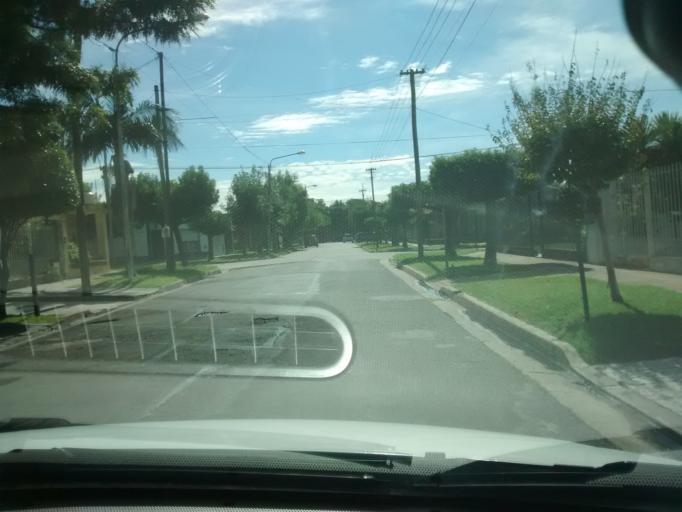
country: AR
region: Buenos Aires
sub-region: Partido de Moron
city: Moron
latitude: -34.6669
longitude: -58.6114
